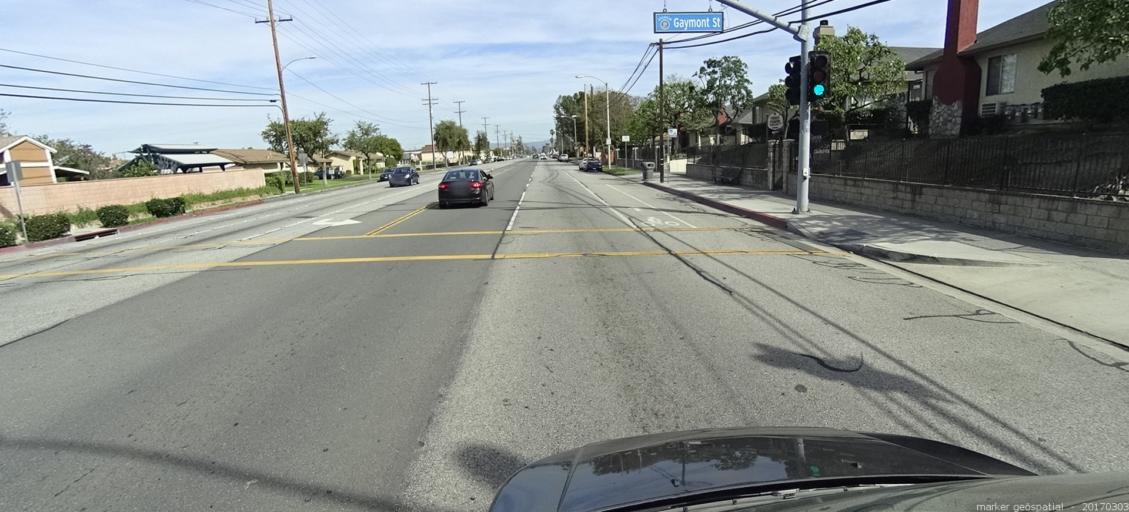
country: US
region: California
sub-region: Orange County
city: Stanton
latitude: 33.8174
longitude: -117.9902
